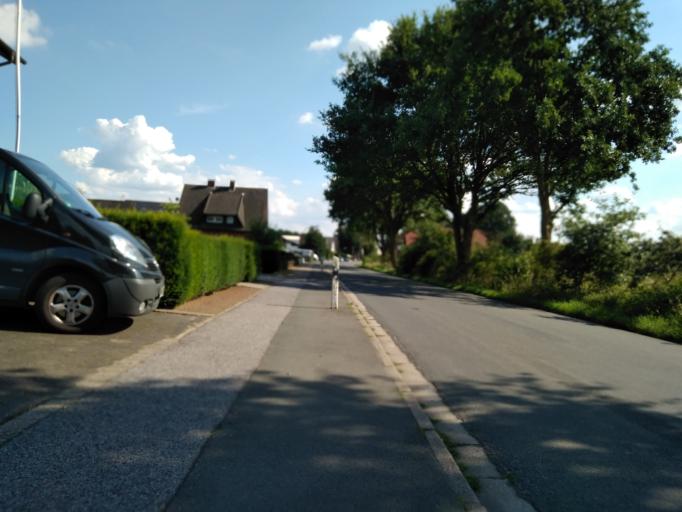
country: DE
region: North Rhine-Westphalia
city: Dorsten
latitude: 51.7085
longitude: 6.9681
